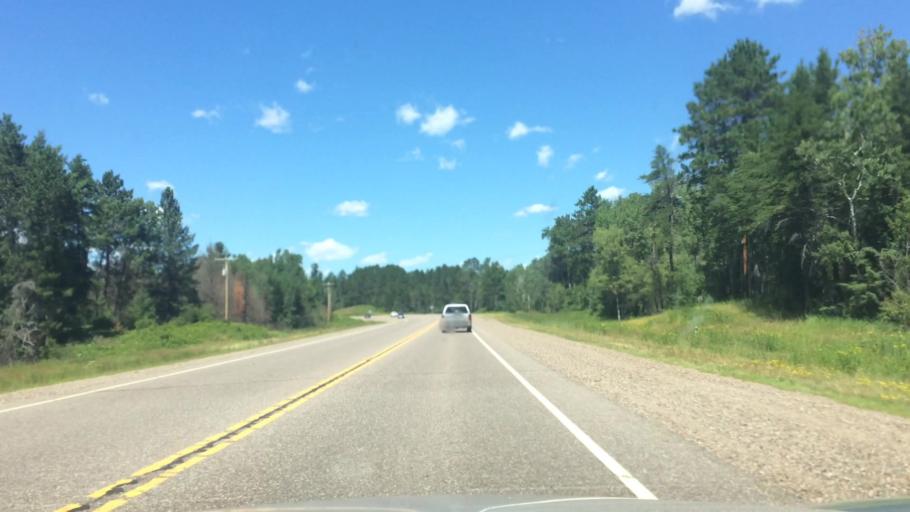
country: US
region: Wisconsin
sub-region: Lincoln County
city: Tomahawk
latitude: 45.6535
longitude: -89.7049
